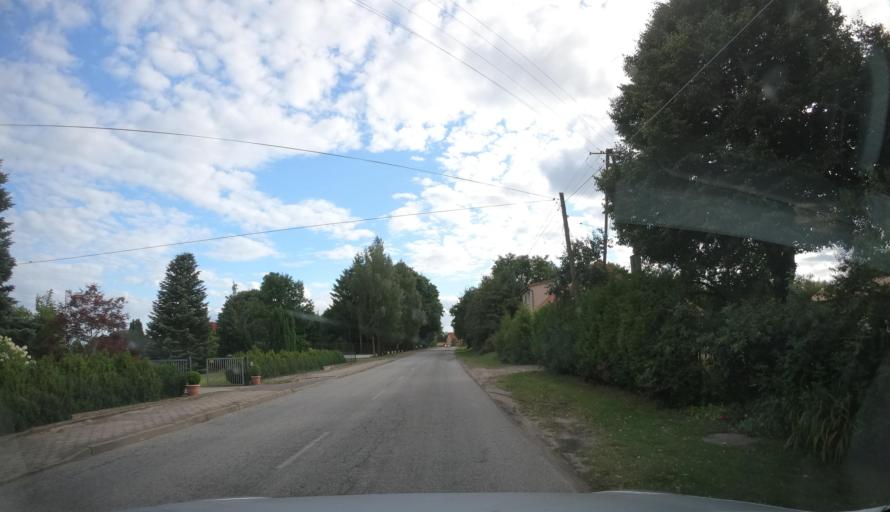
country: PL
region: West Pomeranian Voivodeship
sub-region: Powiat slawienski
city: Slawno
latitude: 54.3223
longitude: 16.6872
